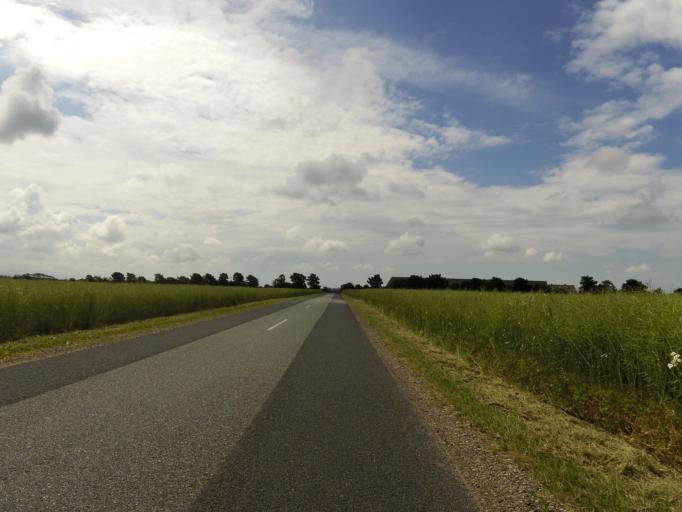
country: DK
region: South Denmark
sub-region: Tonder Kommune
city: Sherrebek
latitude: 55.2060
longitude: 8.8669
